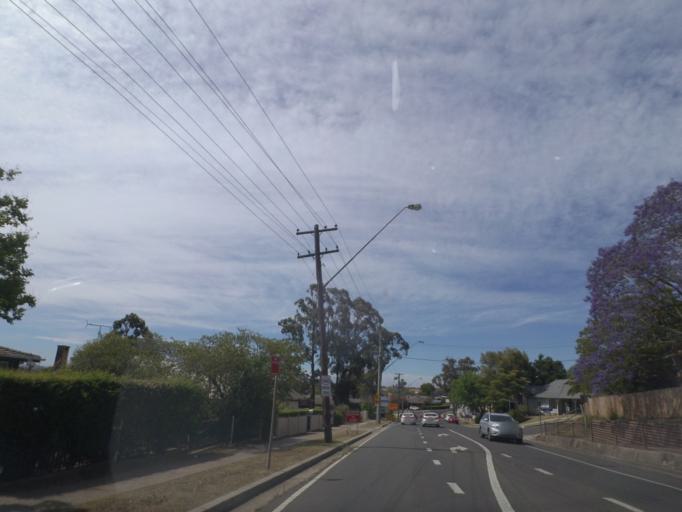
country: AU
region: New South Wales
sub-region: Camden
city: Elderslie
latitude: -34.0585
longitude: 150.6938
